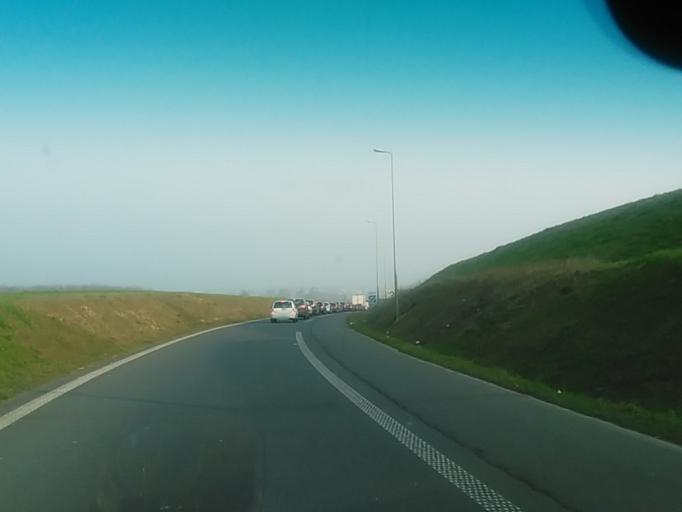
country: FR
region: Lower Normandy
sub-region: Departement du Calvados
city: Eterville
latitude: 49.1505
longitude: -0.4148
